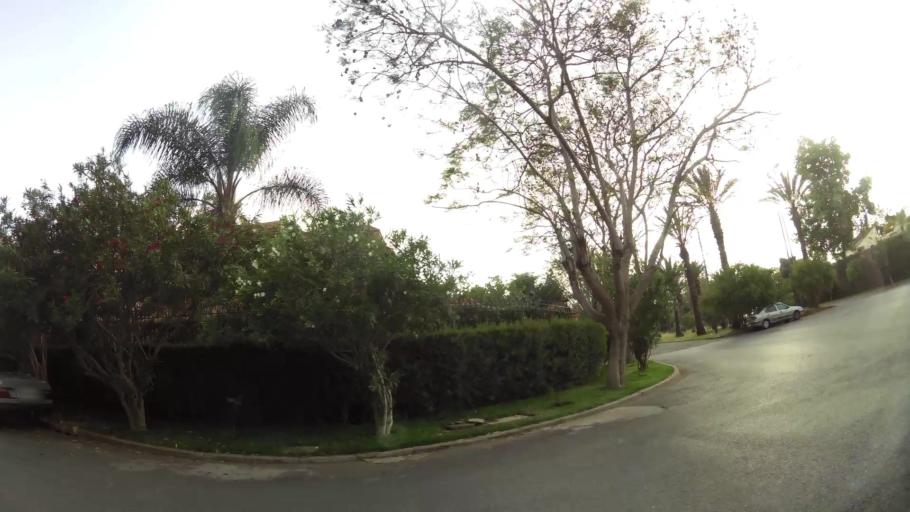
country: MA
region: Rabat-Sale-Zemmour-Zaer
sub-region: Rabat
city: Rabat
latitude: 33.9478
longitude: -6.8194
